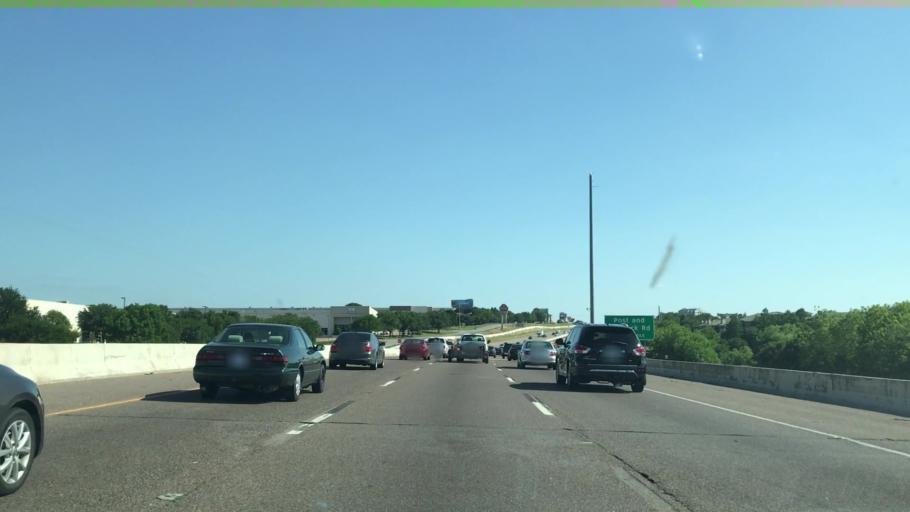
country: US
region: Texas
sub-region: Tarrant County
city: Euless
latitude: 32.8055
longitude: -97.0540
